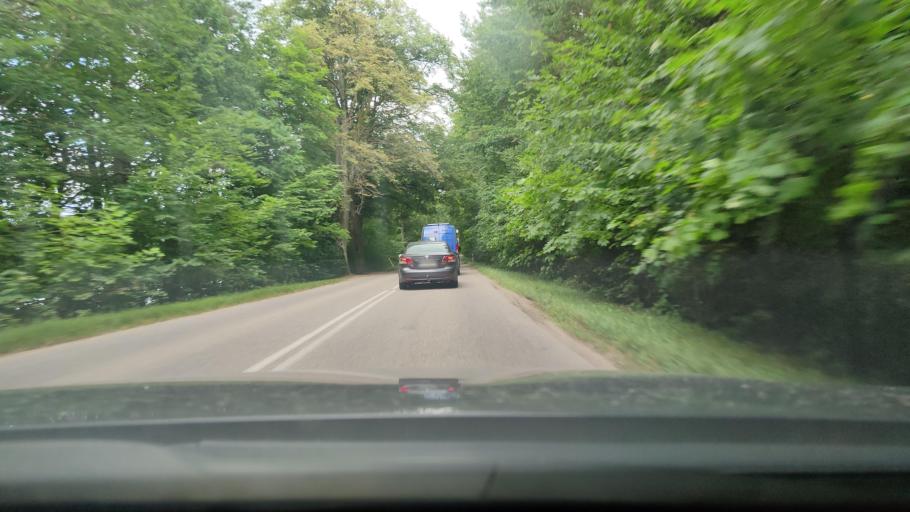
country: PL
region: Pomeranian Voivodeship
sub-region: Powiat pucki
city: Krokowa
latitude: 54.7139
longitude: 18.1653
